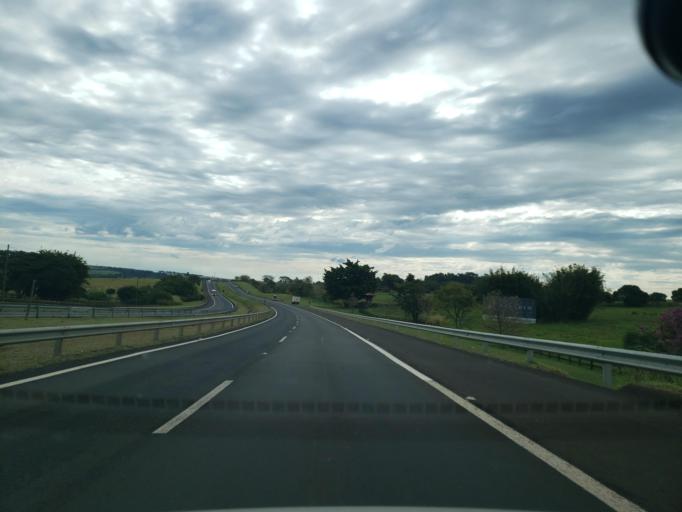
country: BR
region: Sao Paulo
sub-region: Bauru
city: Bauru
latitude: -22.2187
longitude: -49.1677
